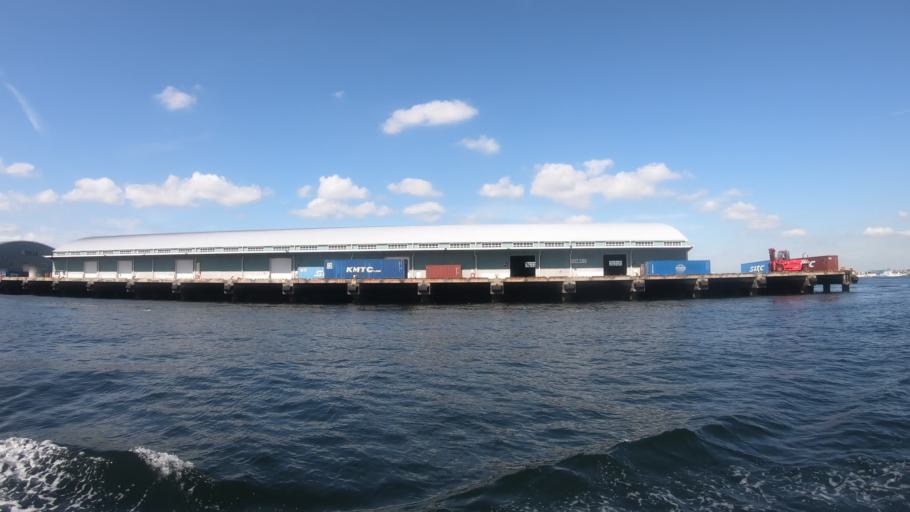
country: JP
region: Kanagawa
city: Yokohama
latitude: 35.4488
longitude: 139.6660
